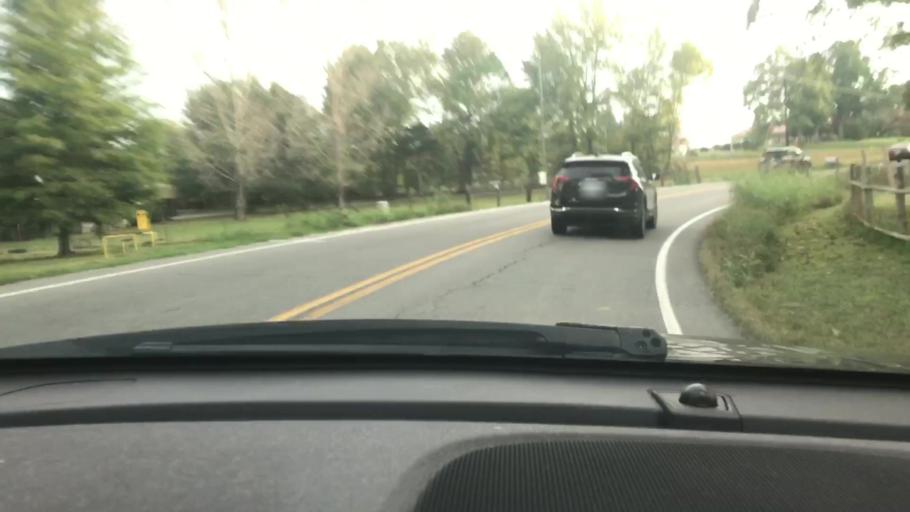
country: US
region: Tennessee
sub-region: Cheatham County
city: Ashland City
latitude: 36.2682
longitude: -87.2165
